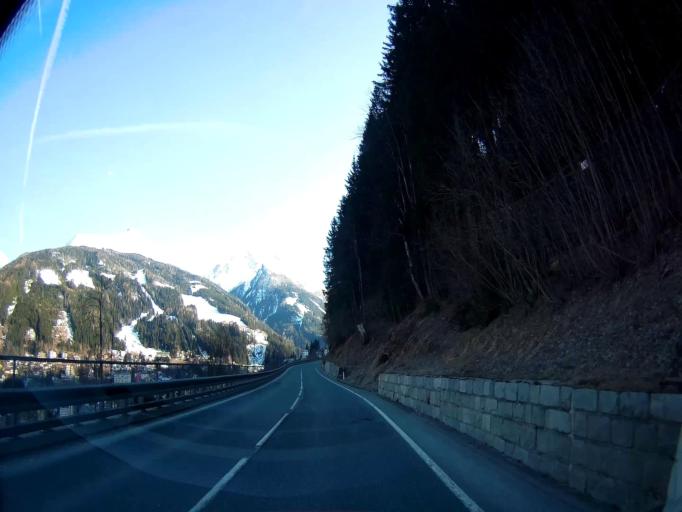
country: AT
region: Salzburg
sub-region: Politischer Bezirk Sankt Johann im Pongau
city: Bad Gastein
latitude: 47.1279
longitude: 13.1305
